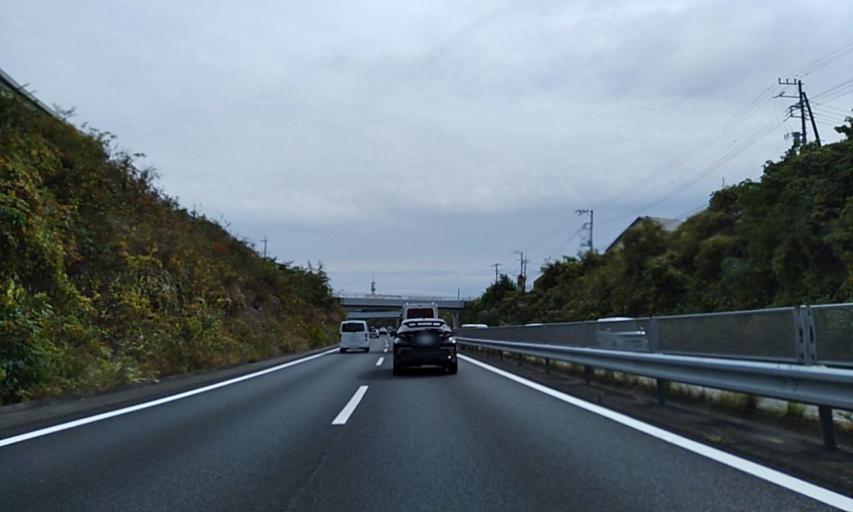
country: JP
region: Shizuoka
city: Fujinomiya
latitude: 35.2075
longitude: 138.6513
